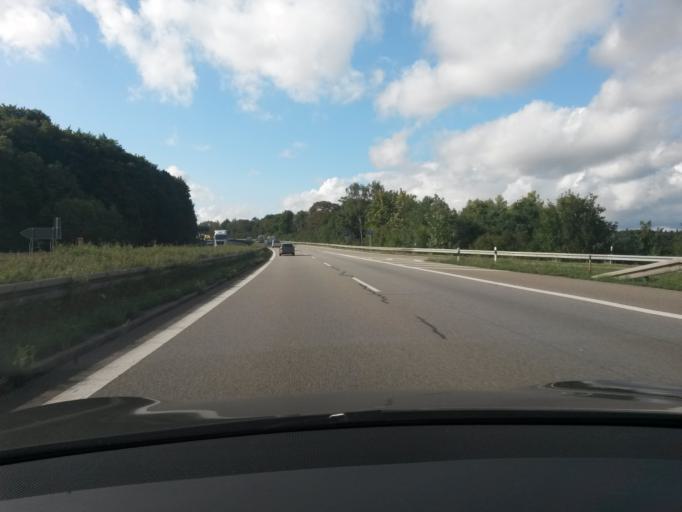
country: DE
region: Bavaria
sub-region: Upper Palatinate
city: Nittendorf
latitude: 49.0293
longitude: 11.9512
